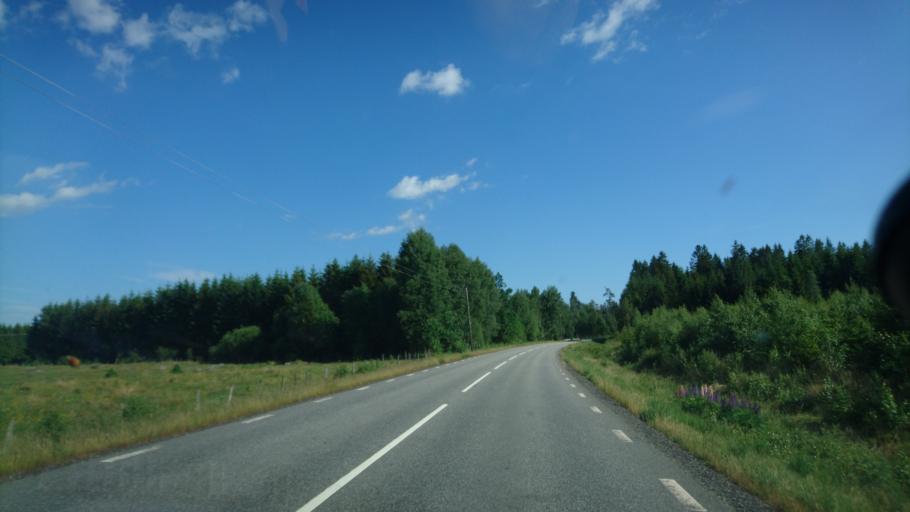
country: SE
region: Skane
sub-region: Osby Kommun
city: Lonsboda
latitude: 56.4655
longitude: 14.2315
